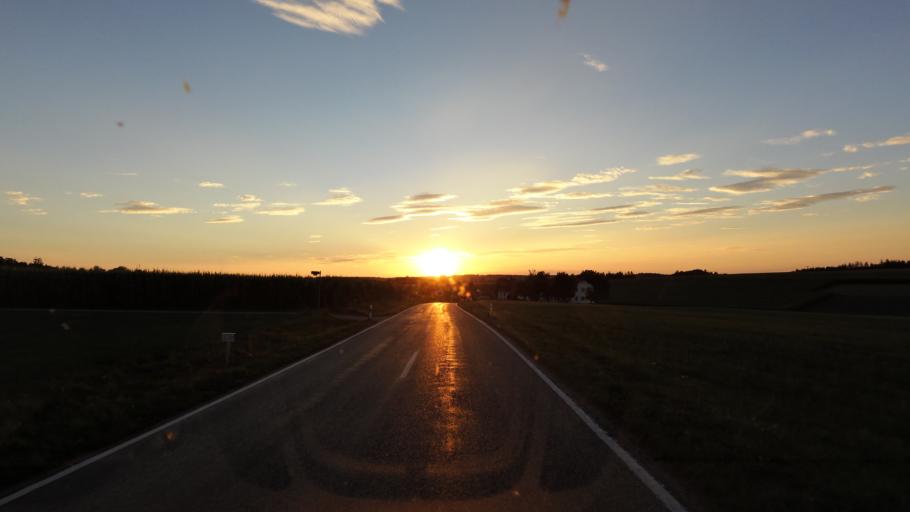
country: DE
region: Bavaria
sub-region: Upper Bavaria
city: Taufkirchen
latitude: 48.1094
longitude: 12.4736
